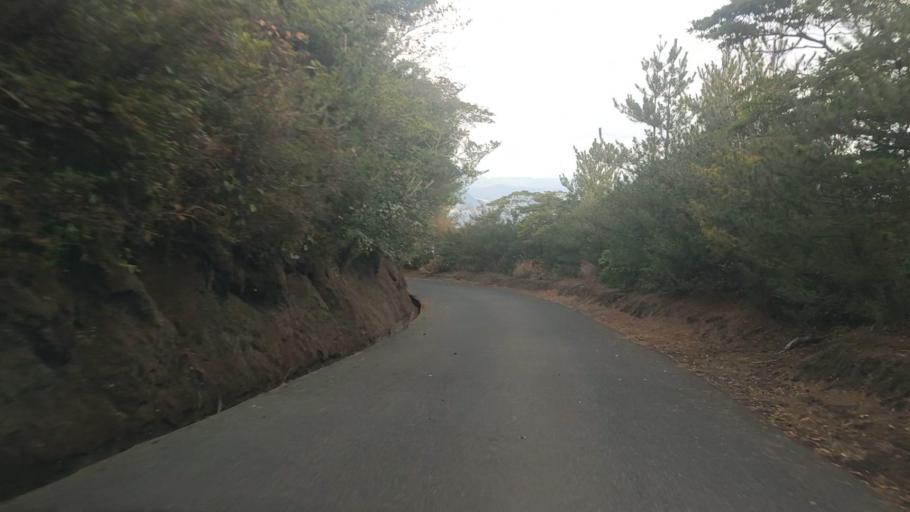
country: JP
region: Kagoshima
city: Kagoshima-shi
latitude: 31.5936
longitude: 130.6352
